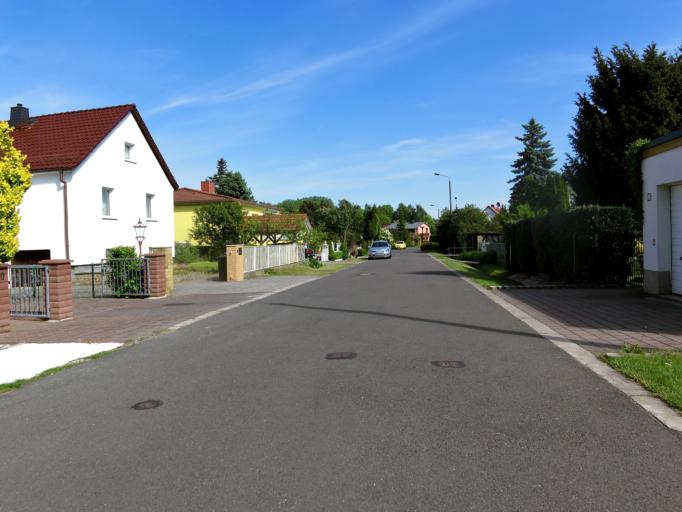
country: DE
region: Saxony
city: Leipzig
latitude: 51.3172
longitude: 12.4326
